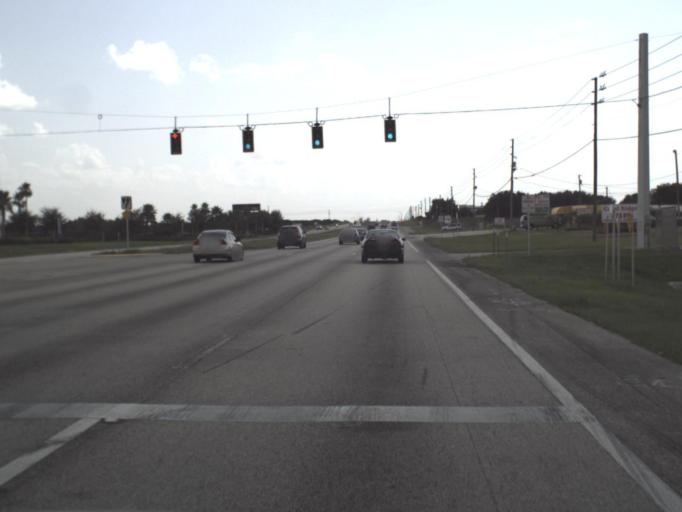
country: US
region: Florida
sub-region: Polk County
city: Davenport
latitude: 28.1942
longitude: -81.6400
